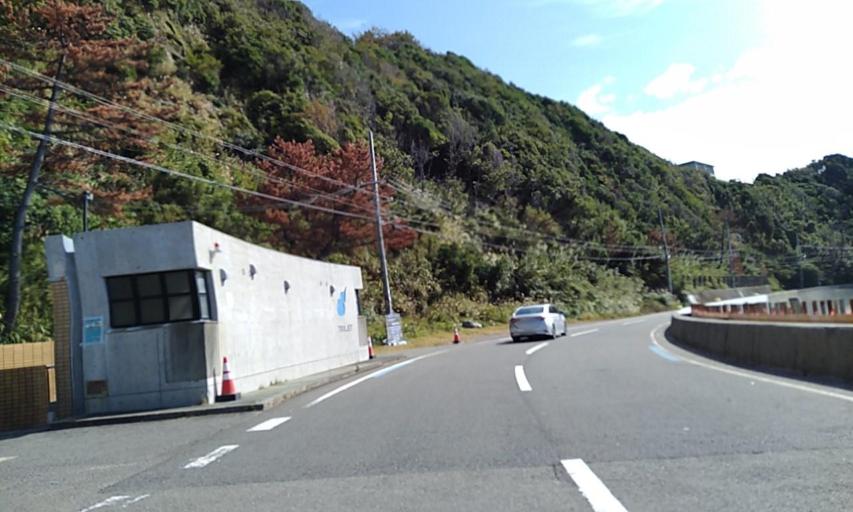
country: JP
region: Wakayama
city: Gobo
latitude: 33.9721
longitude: 135.0791
